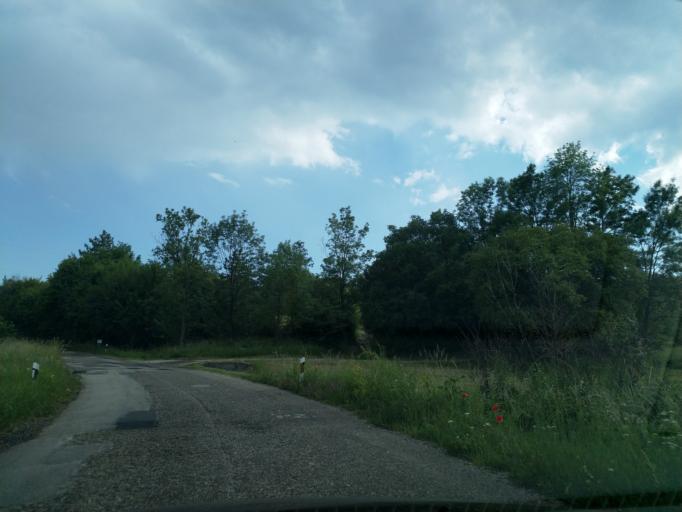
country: RS
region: Central Serbia
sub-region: Zajecarski Okrug
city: Boljevac
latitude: 43.9799
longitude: 21.9726
